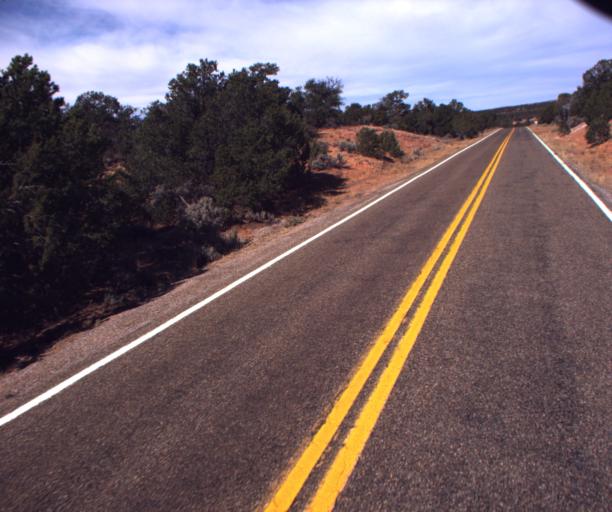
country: US
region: Arizona
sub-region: Navajo County
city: Kayenta
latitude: 36.6045
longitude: -110.4994
